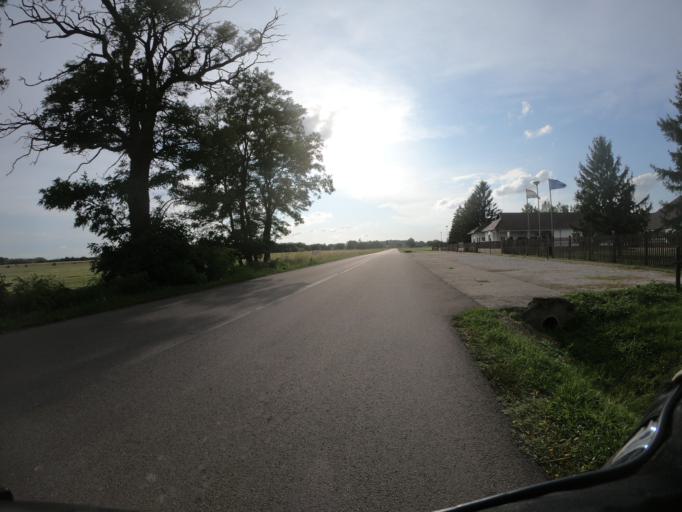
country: HU
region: Borsod-Abauj-Zemplen
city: Mezokeresztes
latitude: 47.8304
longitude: 20.7913
